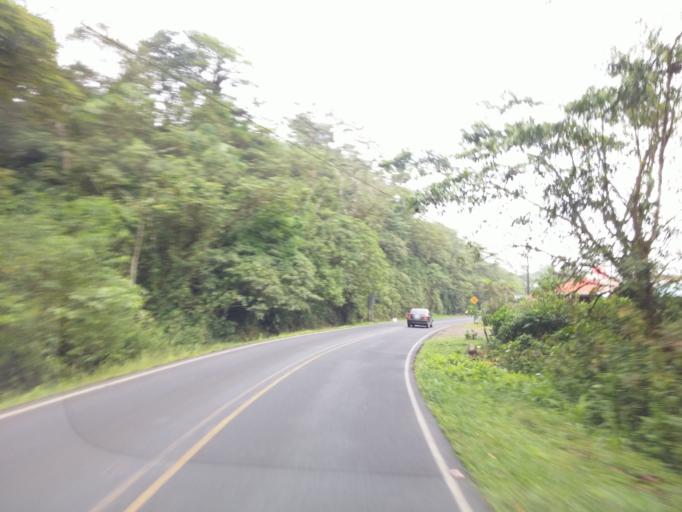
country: CR
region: Alajuela
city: San Ramon
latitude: 10.1963
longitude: -84.5195
